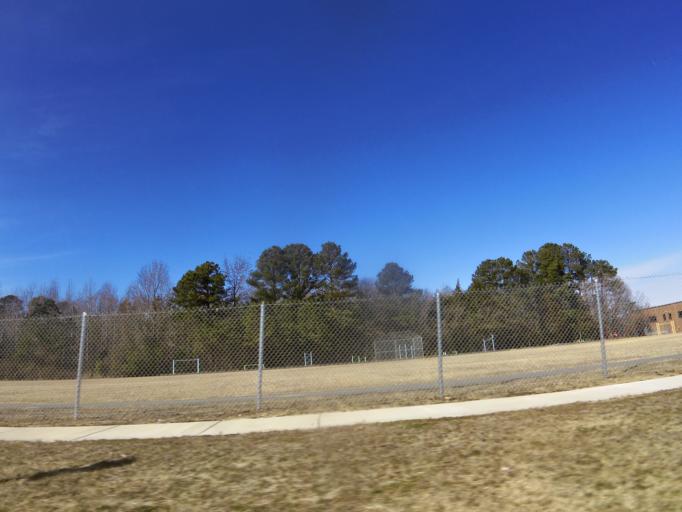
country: US
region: Virginia
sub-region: Isle of Wight County
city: Smithfield
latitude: 36.9738
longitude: -76.6501
